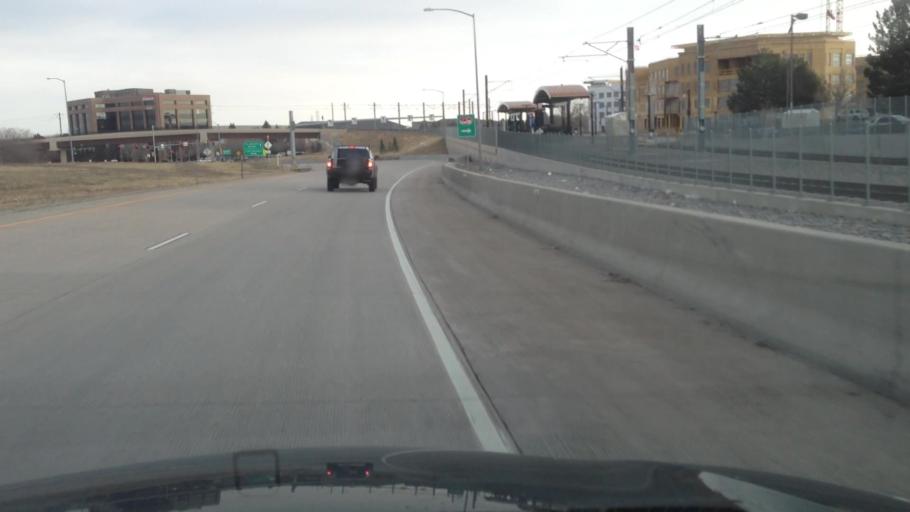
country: US
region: Colorado
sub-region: Adams County
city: Aurora
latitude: 39.6724
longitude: -104.8280
